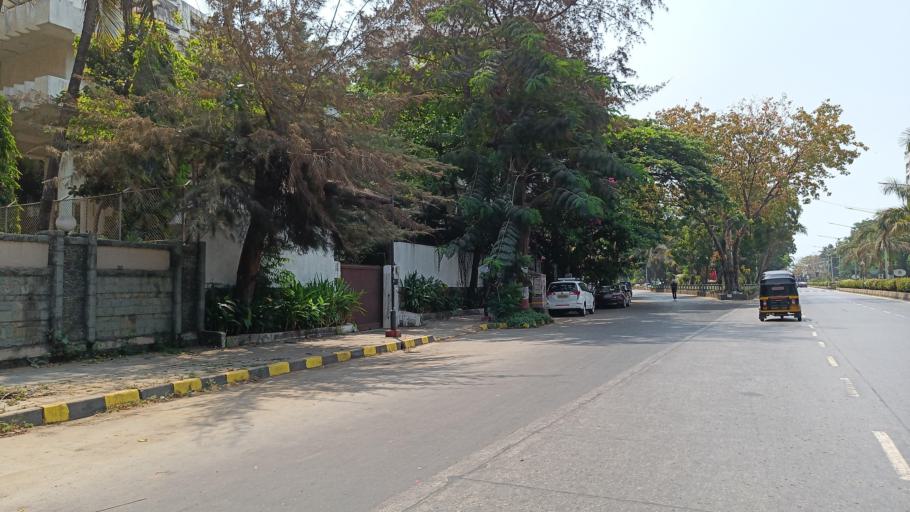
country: IN
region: Maharashtra
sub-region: Mumbai Suburban
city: Mumbai
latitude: 19.1070
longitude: 72.8300
